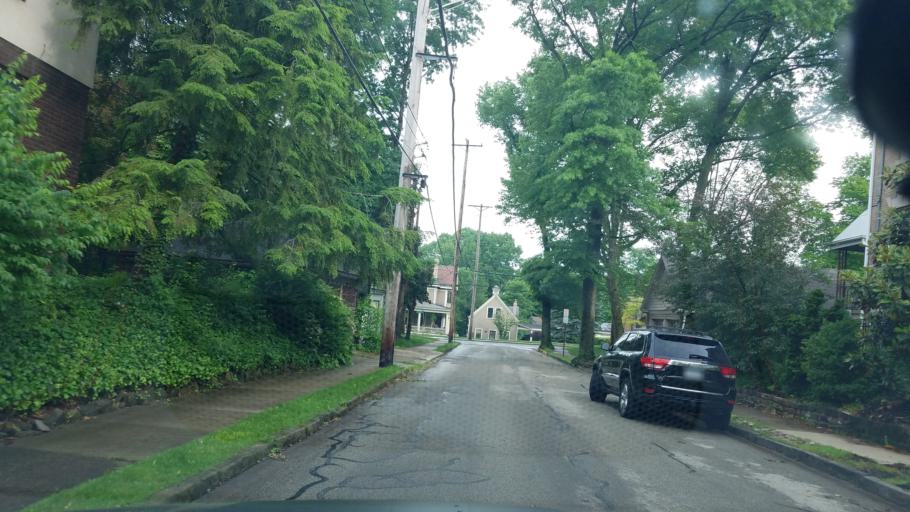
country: US
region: Pennsylvania
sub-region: Allegheny County
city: Edgewood
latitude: 40.4308
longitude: -79.8865
